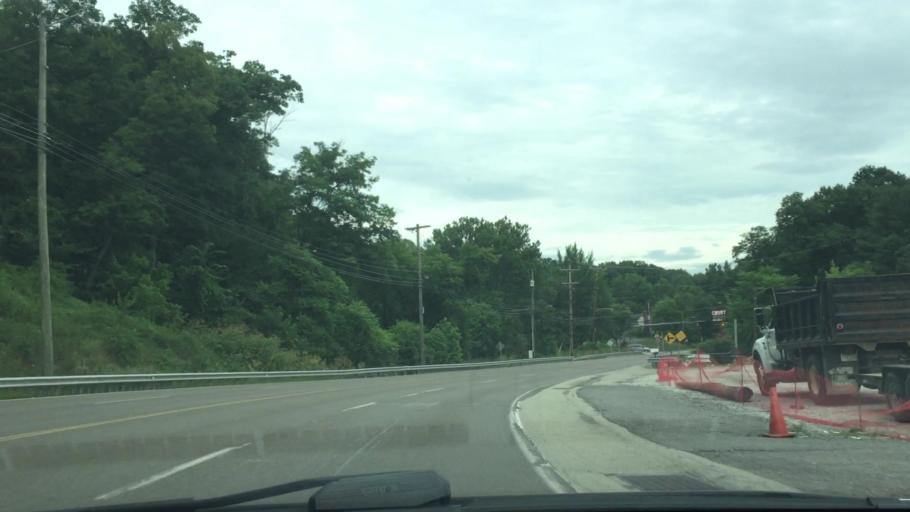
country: US
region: Pennsylvania
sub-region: Allegheny County
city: Mount Lebanon
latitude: 40.3625
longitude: -80.0662
